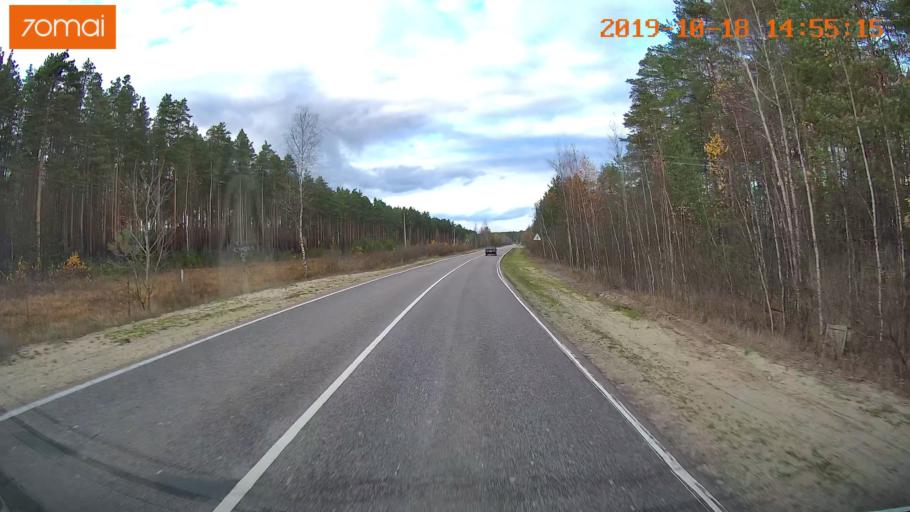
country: RU
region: Vladimir
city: Kurlovo
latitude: 55.4494
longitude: 40.5885
